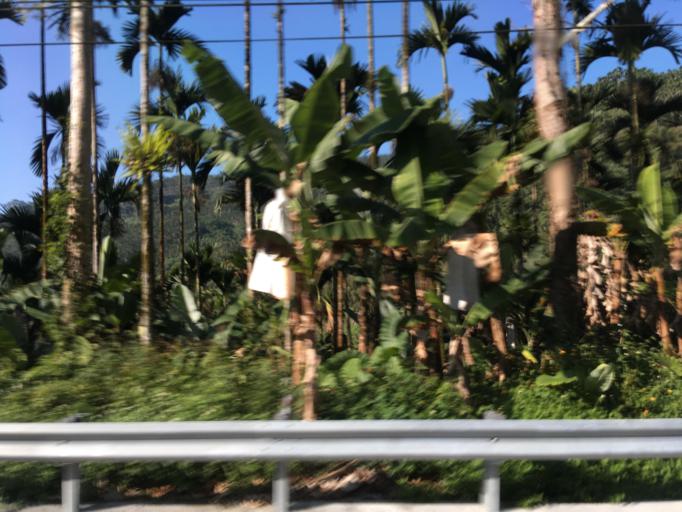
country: TW
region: Taiwan
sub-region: Chiayi
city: Jiayi Shi
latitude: 23.4339
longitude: 120.6401
